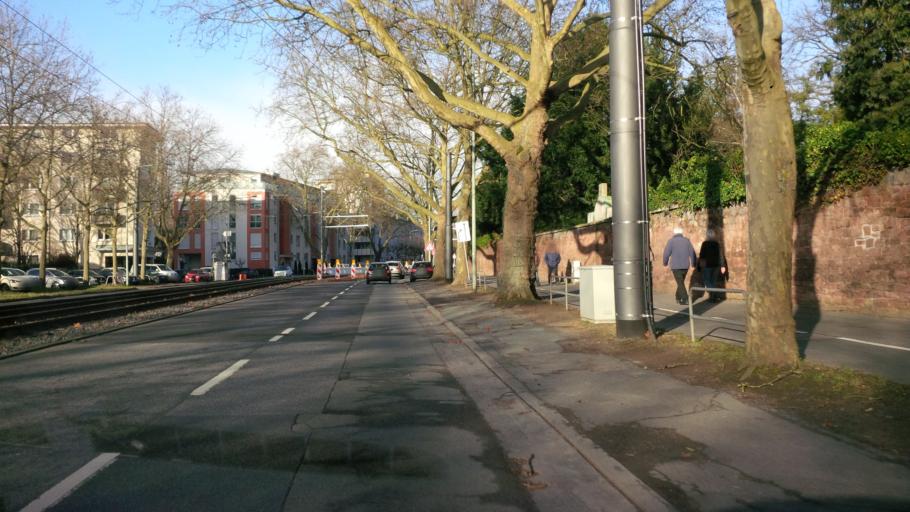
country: DE
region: Hesse
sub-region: Regierungsbezirk Darmstadt
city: Frankfurt am Main
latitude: 50.1342
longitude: 8.6841
